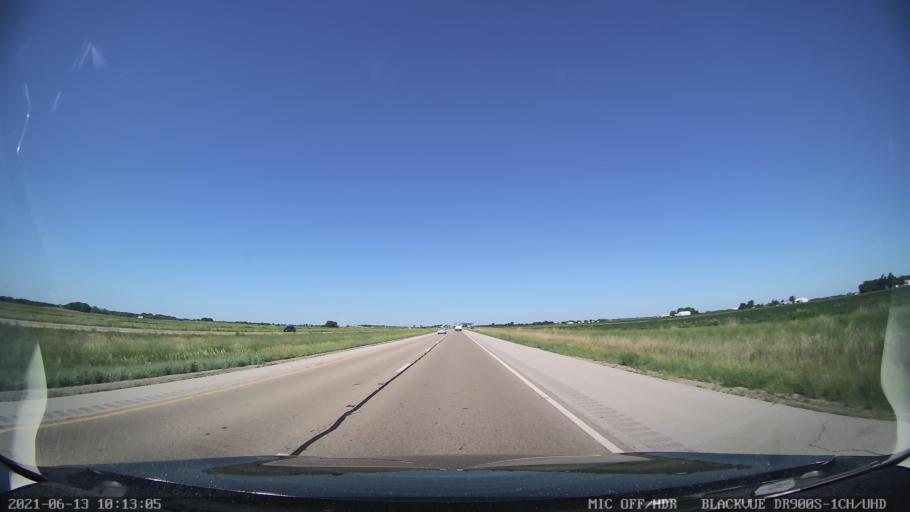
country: US
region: Illinois
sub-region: Logan County
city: Lincoln
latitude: 40.1816
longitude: -89.3973
